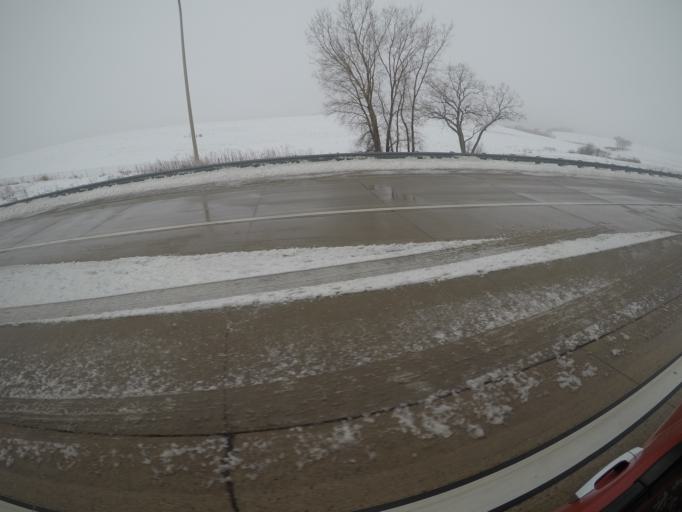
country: US
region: Minnesota
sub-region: Olmsted County
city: Oronoco
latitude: 44.1864
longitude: -92.5828
